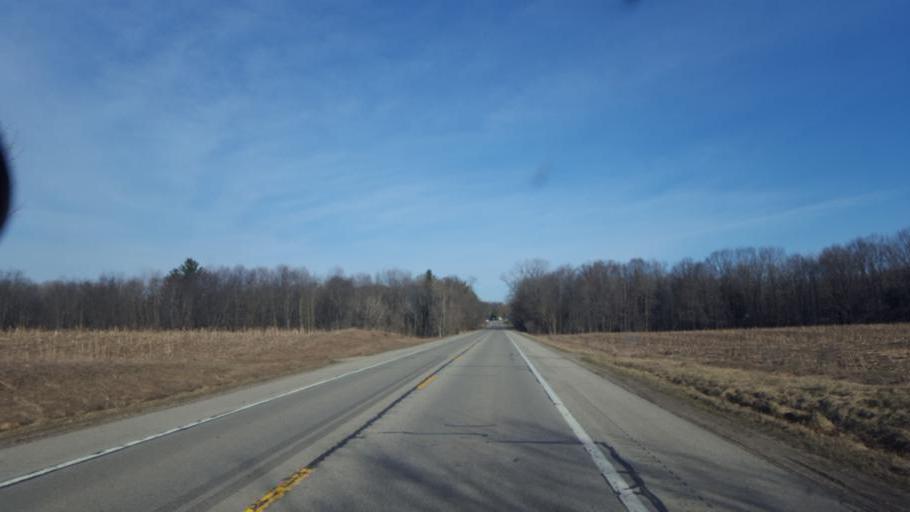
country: US
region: Michigan
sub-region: Montcalm County
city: Edmore
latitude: 43.4216
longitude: -85.1391
